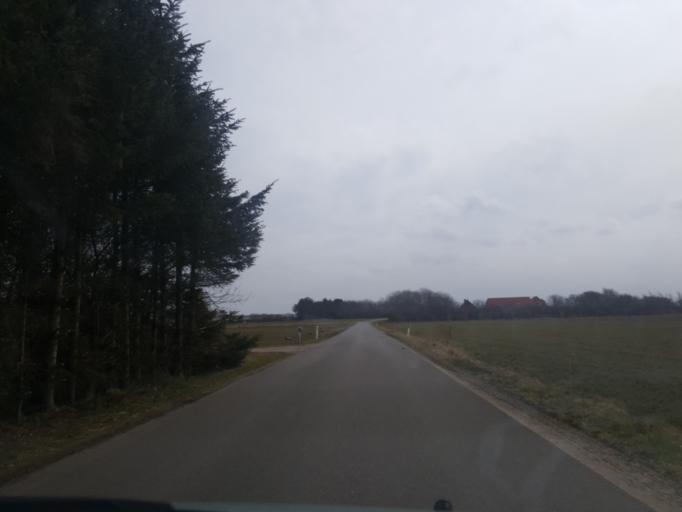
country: DK
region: Central Jutland
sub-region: Ringkobing-Skjern Kommune
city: Ringkobing
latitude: 56.2022
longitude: 8.1937
